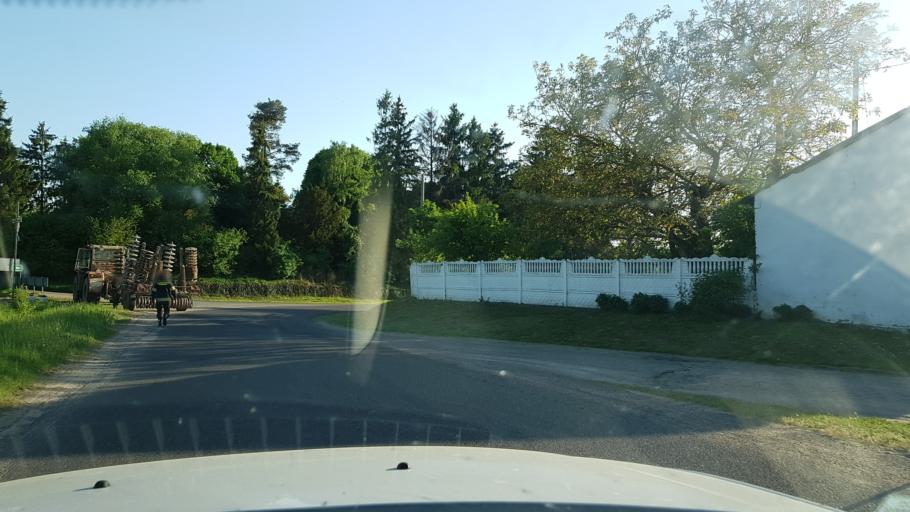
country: PL
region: West Pomeranian Voivodeship
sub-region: Powiat lobeski
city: Dobra
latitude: 53.5656
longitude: 15.1982
